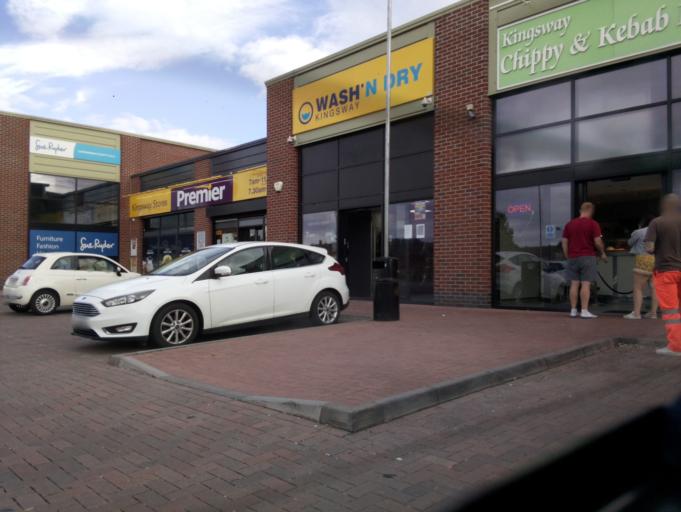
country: GB
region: England
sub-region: Gloucestershire
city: Gloucester
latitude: 51.8204
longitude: -2.2676
